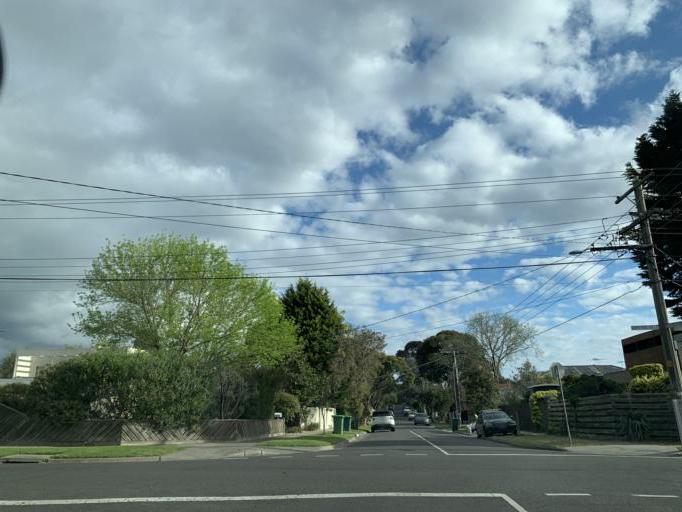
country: AU
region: Victoria
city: Beaumaris
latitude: -37.9850
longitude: 145.0403
